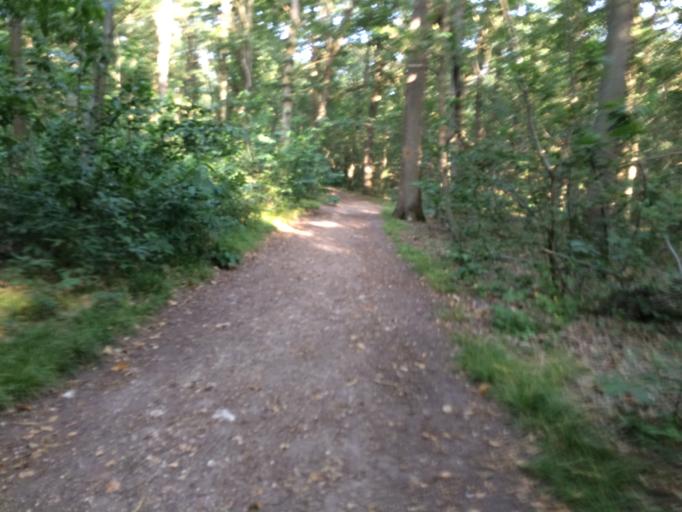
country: FR
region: Ile-de-France
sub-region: Departement de l'Essonne
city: Igny
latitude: 48.7501
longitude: 2.2406
